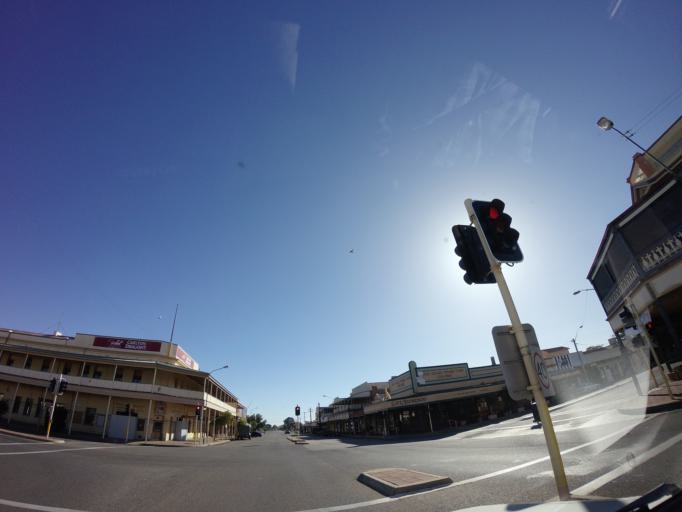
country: AU
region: New South Wales
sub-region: Broken Hill Municipality
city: Broken Hill
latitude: -31.9571
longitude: 141.4675
